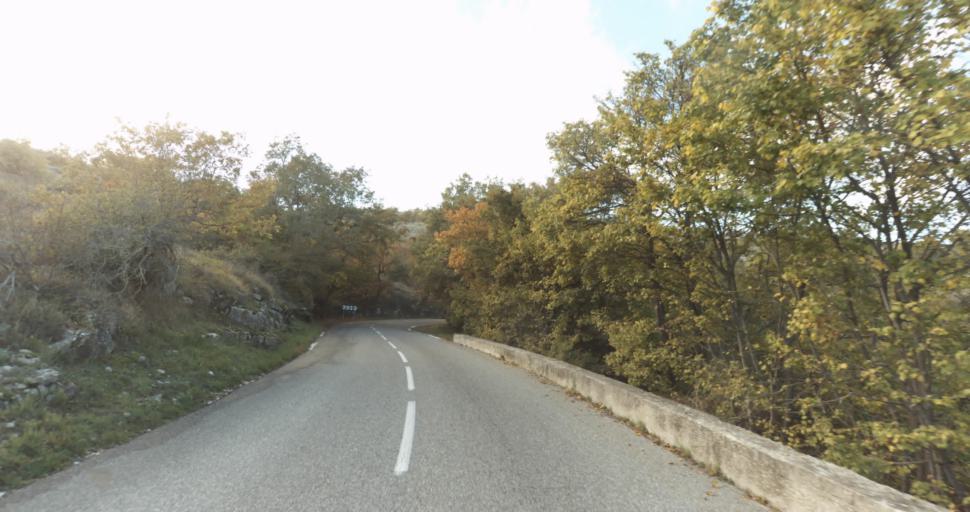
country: FR
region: Provence-Alpes-Cote d'Azur
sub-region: Departement des Alpes-Maritimes
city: Vence
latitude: 43.7605
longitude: 7.0846
